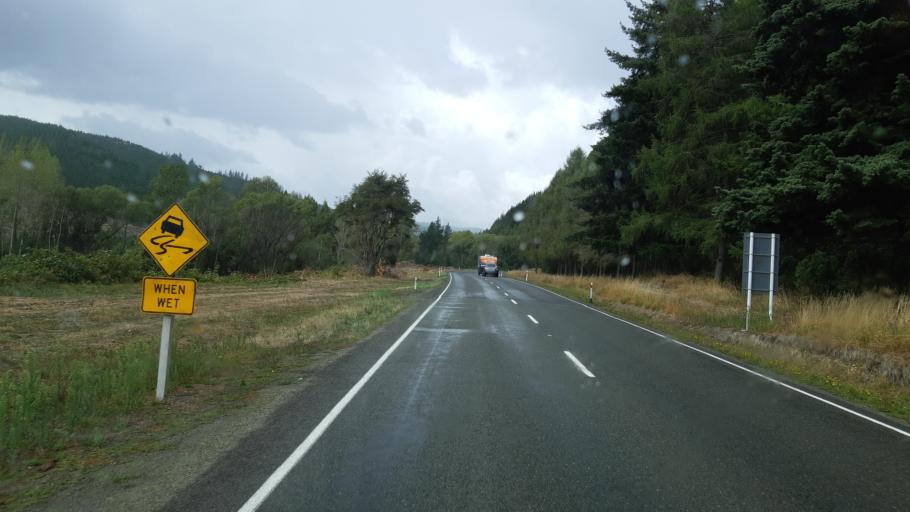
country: NZ
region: Tasman
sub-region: Tasman District
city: Wakefield
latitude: -41.4747
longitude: 172.8482
